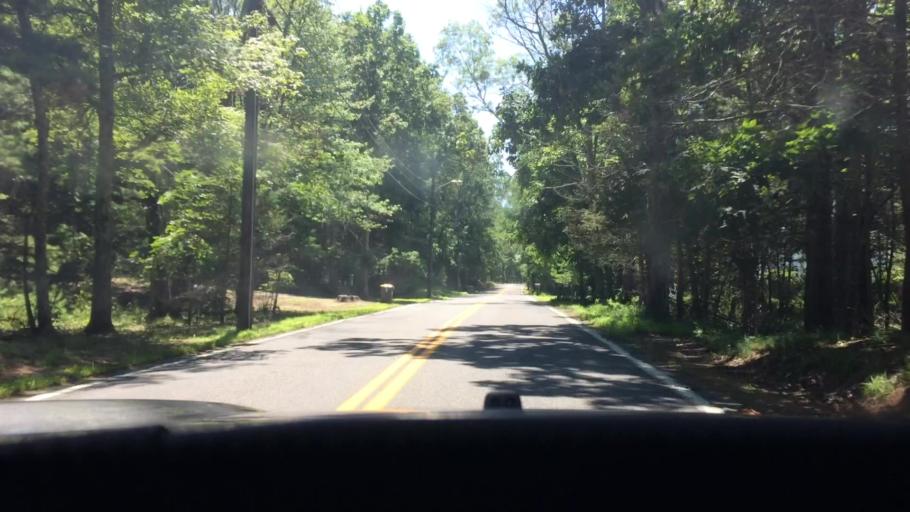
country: US
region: Rhode Island
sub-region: Providence County
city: Harrisville
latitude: 41.9877
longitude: -71.6829
